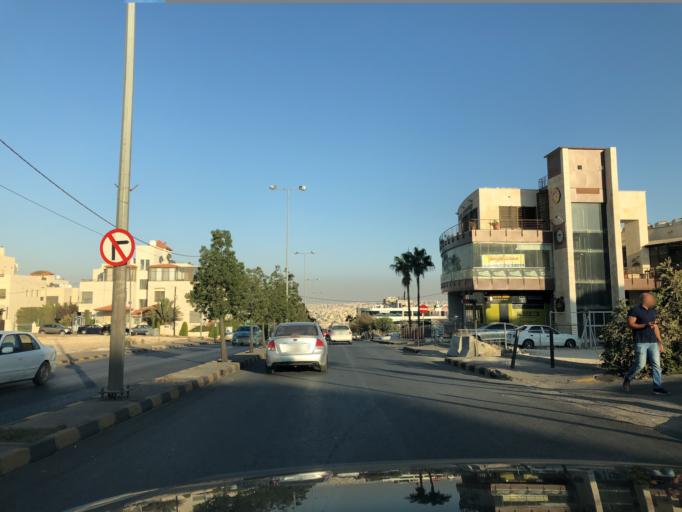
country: JO
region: Amman
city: Al Bunayyat ash Shamaliyah
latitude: 31.9418
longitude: 35.8822
